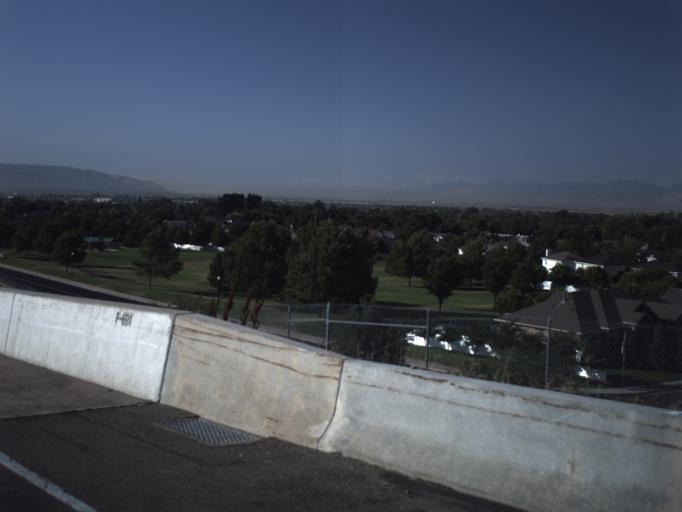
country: US
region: Utah
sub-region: Davis County
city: Fruit Heights
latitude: 41.0101
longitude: -111.9129
